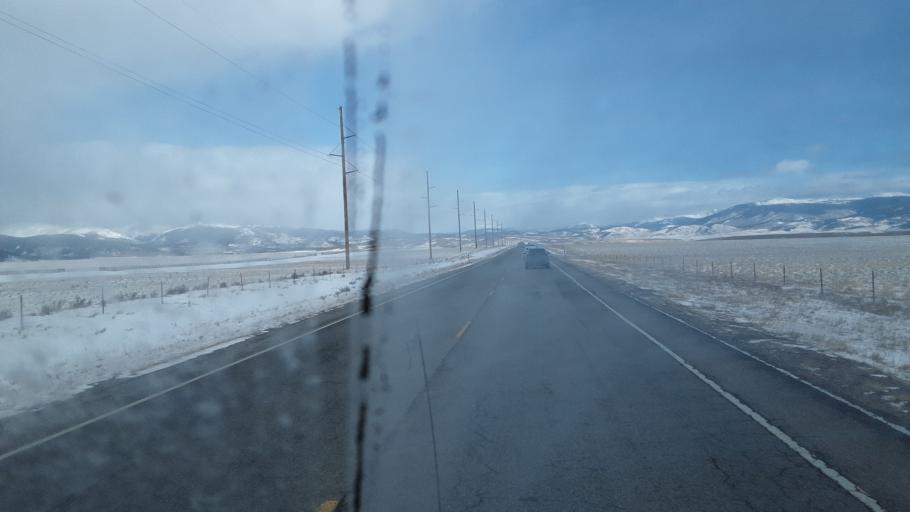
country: US
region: Colorado
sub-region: Park County
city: Fairplay
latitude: 39.3230
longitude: -105.8754
